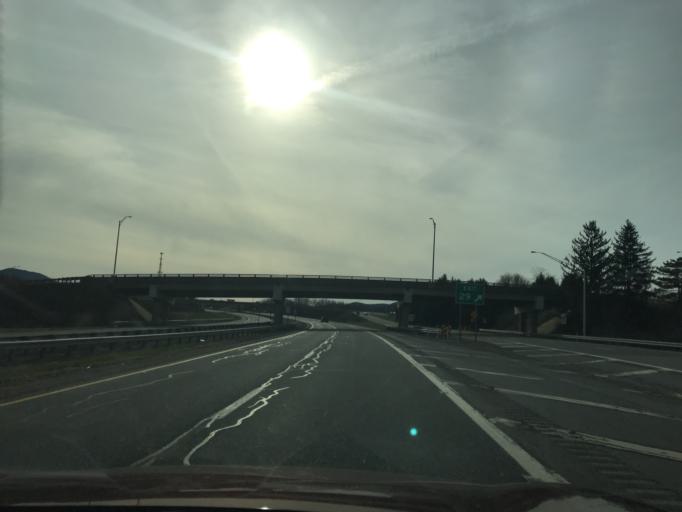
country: US
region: Pennsylvania
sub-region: Lycoming County
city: Duboistown
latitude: 41.2317
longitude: -77.0357
